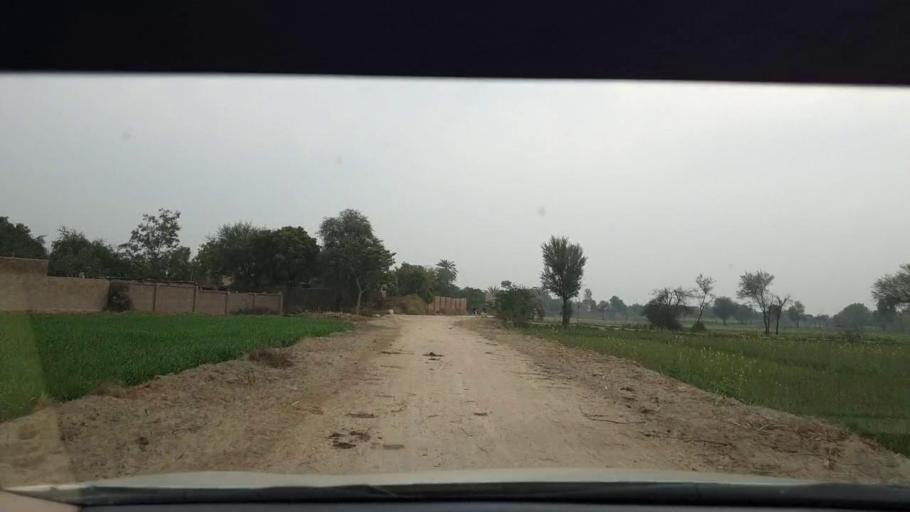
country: PK
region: Sindh
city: Berani
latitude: 25.8561
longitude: 68.7991
